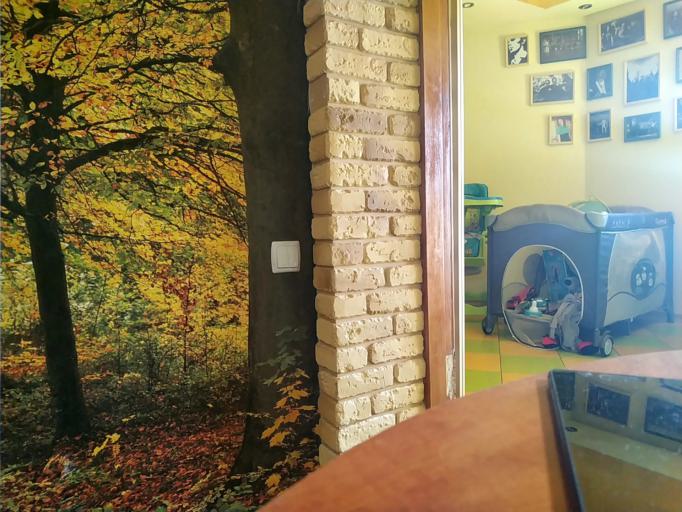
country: RU
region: Tverskaya
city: Vyshniy Volochek
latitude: 57.5733
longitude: 34.5726
